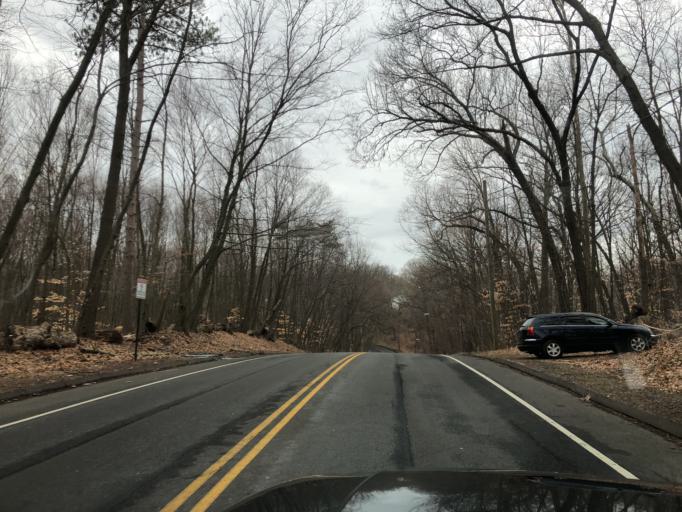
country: US
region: Connecticut
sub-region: Hartford County
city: New Britain
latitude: 41.6961
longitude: -72.7792
